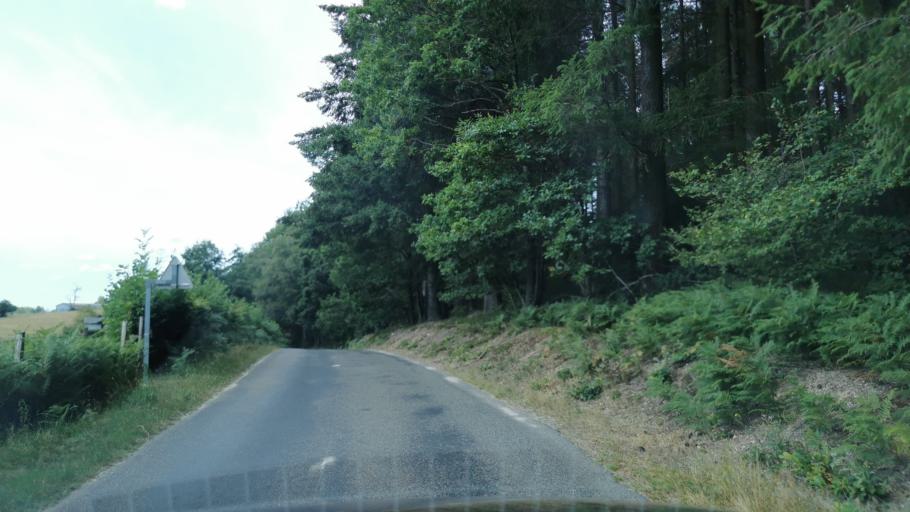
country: FR
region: Bourgogne
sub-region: Departement de Saone-et-Loire
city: Marmagne
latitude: 46.8106
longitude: 4.2847
